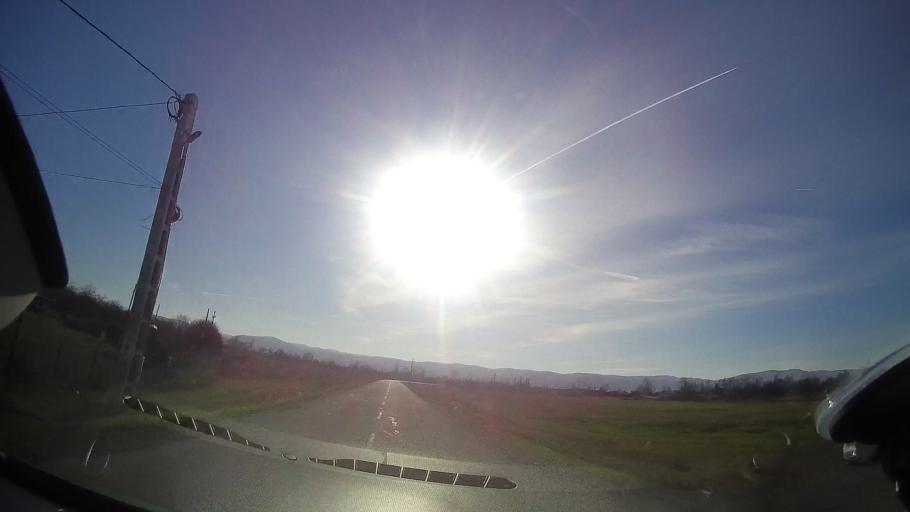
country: RO
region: Bihor
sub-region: Comuna Auseu
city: Auseu
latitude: 47.0313
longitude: 22.4935
